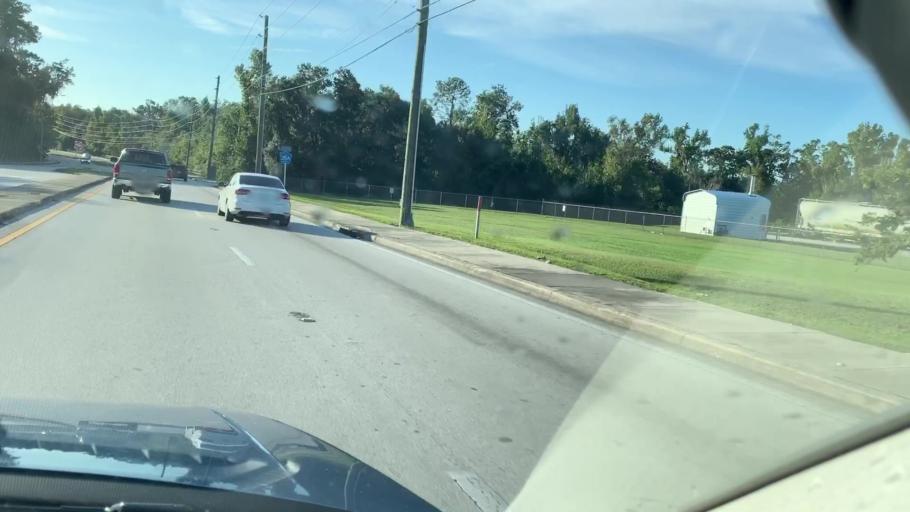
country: US
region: Florida
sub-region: Polk County
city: Gibsonia
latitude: 28.0792
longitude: -81.9940
